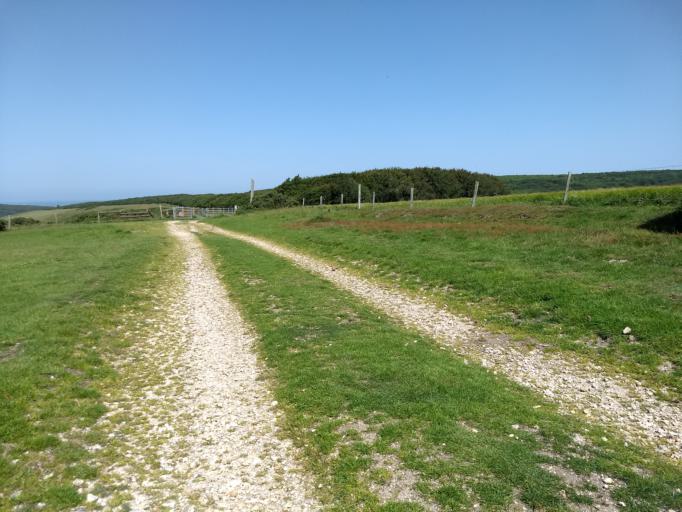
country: GB
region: England
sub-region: Isle of Wight
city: Shalfleet
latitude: 50.6523
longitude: -1.3837
